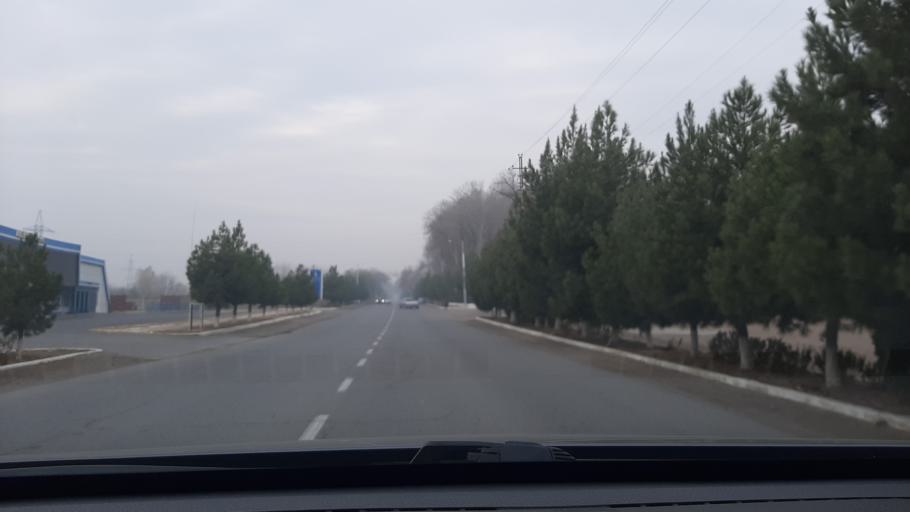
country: TJ
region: Viloyati Sughd
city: Palos
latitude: 40.2702
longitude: 69.8104
